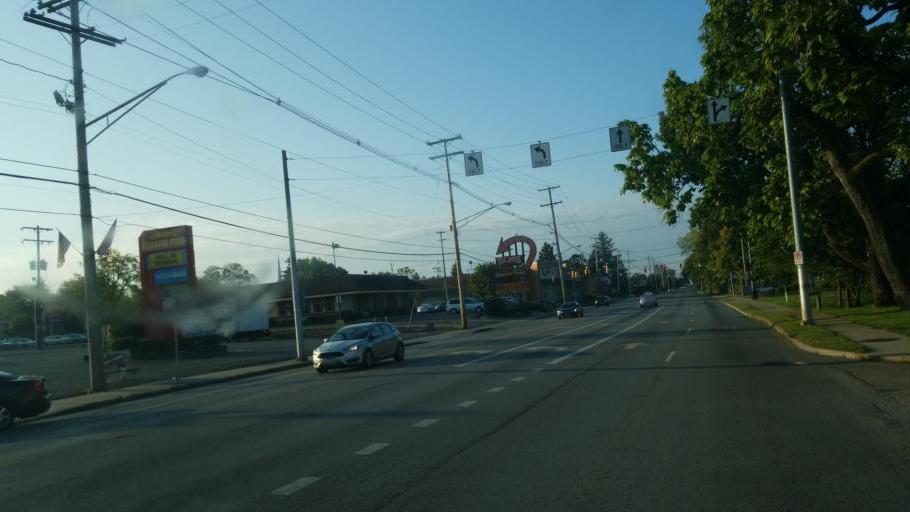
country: US
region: Ohio
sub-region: Franklin County
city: Worthington
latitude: 40.0635
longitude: -83.0195
